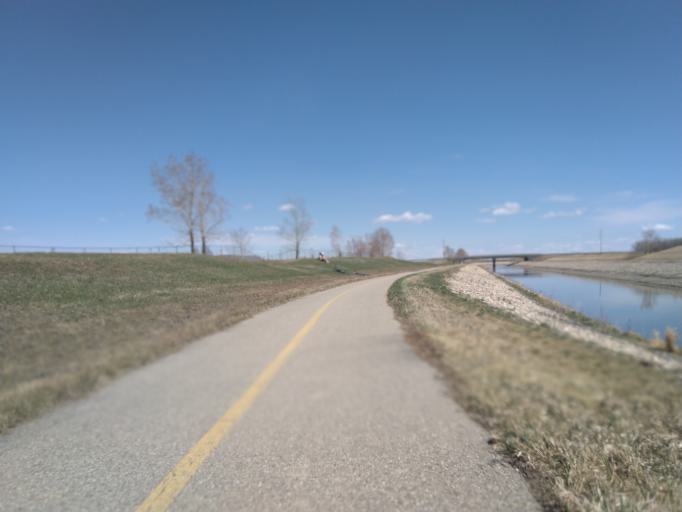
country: CA
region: Alberta
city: Chestermere
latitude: 50.9703
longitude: -113.9416
